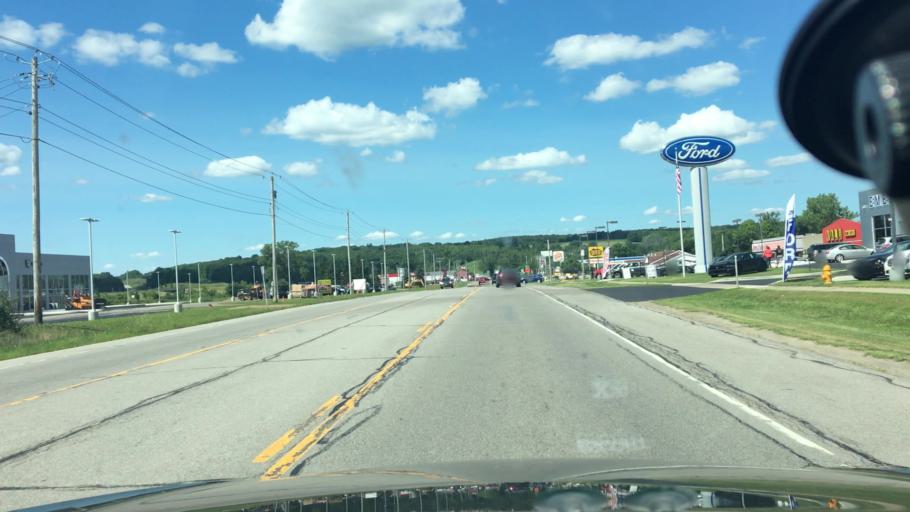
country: US
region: New York
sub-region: Erie County
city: Springville
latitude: 42.5050
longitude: -78.6894
